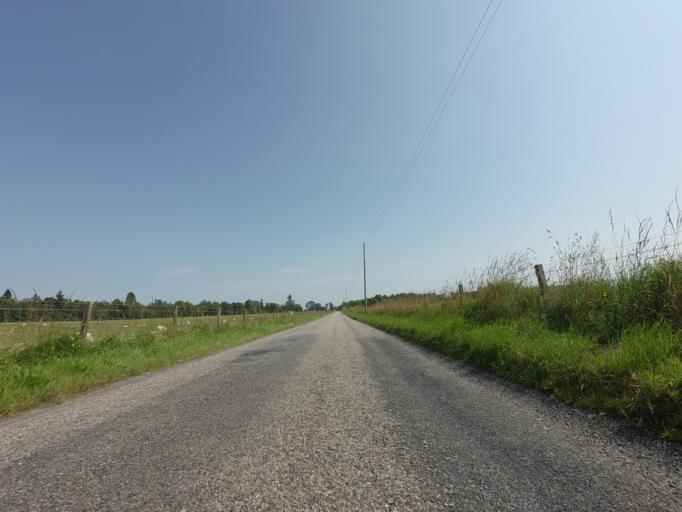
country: GB
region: Scotland
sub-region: Highland
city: Tain
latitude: 57.7941
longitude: -4.0778
